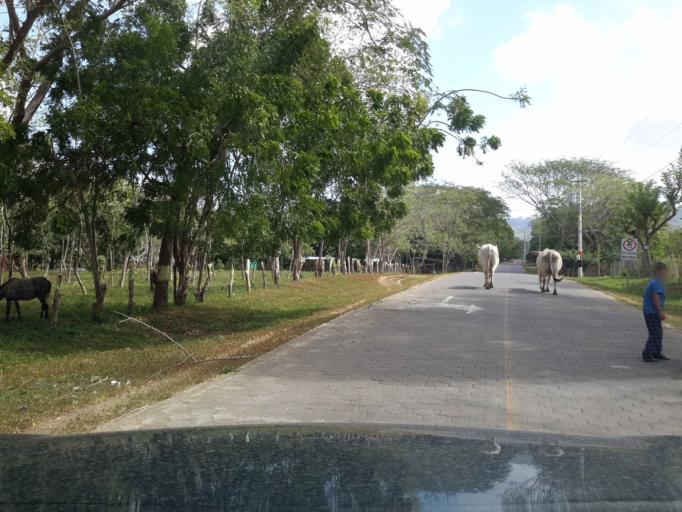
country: NI
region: Rivas
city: San Juan del Sur
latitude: 11.2443
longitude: -85.8451
